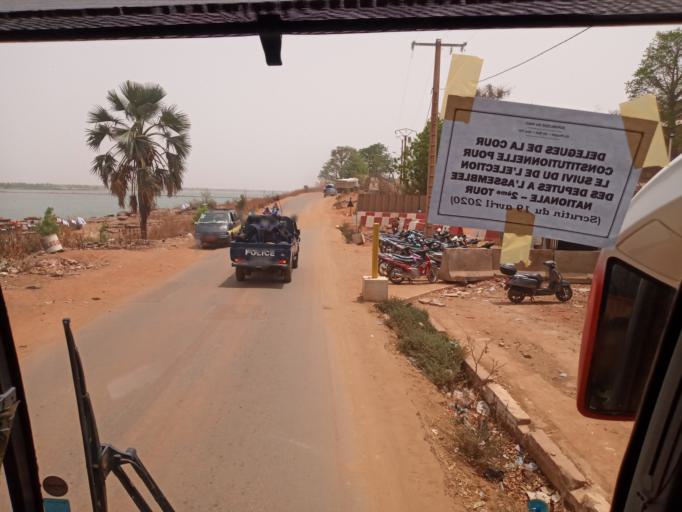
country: ML
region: Koulikoro
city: Koulikoro
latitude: 12.8854
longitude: -7.5427
